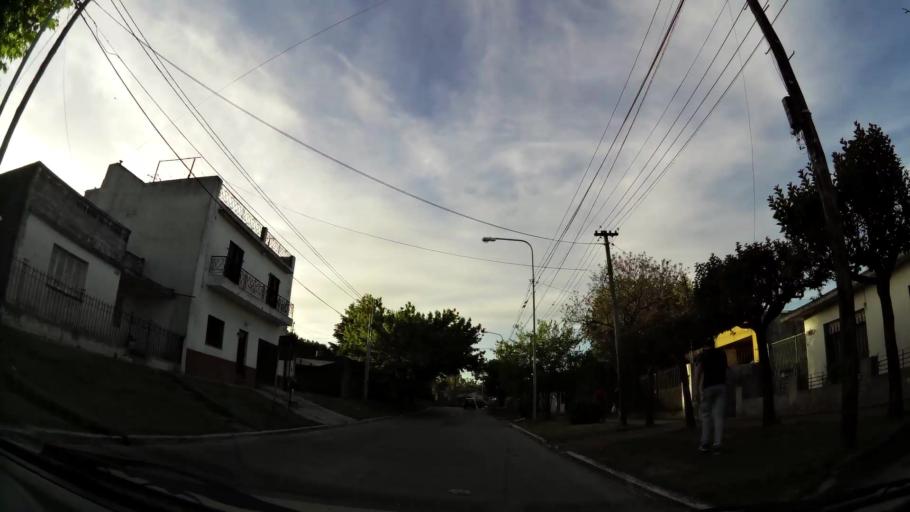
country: AR
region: Buenos Aires
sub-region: Partido de Quilmes
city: Quilmes
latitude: -34.7795
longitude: -58.1942
